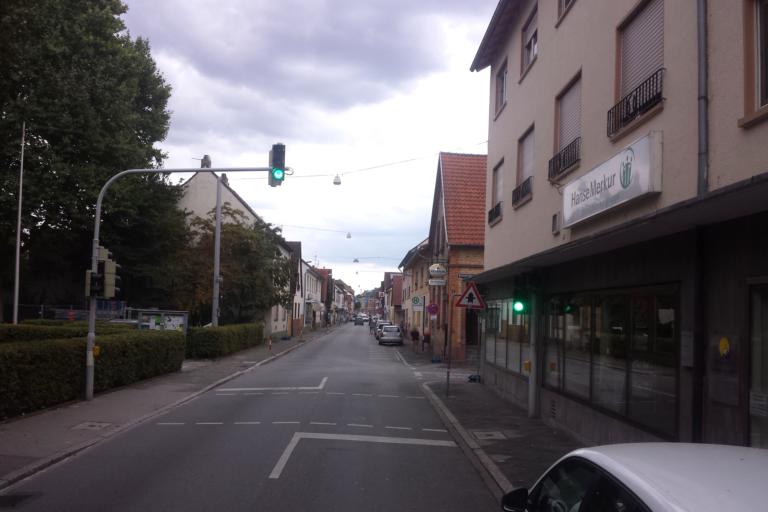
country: DE
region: Hesse
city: Lampertheim
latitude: 49.5460
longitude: 8.4467
